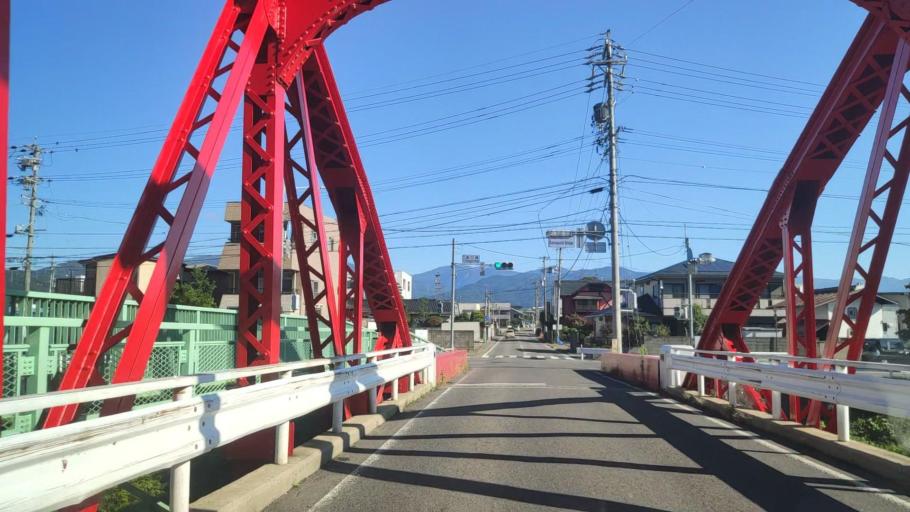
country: JP
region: Nagano
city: Okaya
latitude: 36.0541
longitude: 138.0508
